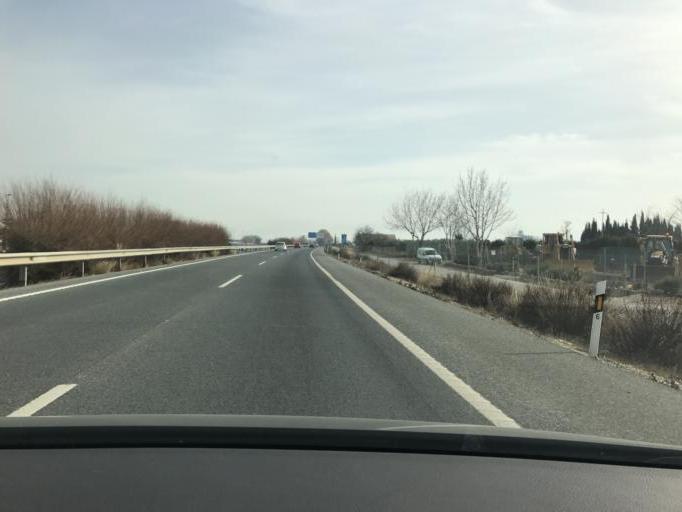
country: ES
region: Andalusia
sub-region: Provincia de Granada
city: Chauchina
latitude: 37.1918
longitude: -3.7866
